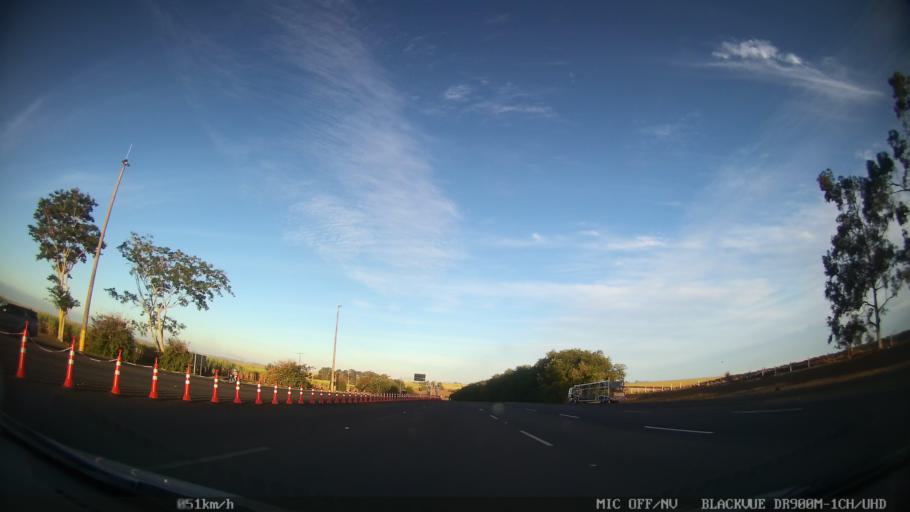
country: BR
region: Sao Paulo
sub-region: Catanduva
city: Catanduva
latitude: -21.0698
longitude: -49.1033
